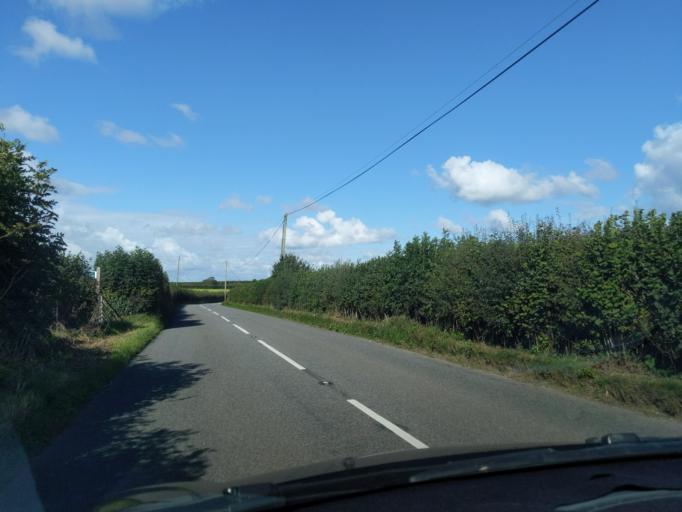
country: GB
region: England
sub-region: Cornwall
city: Boyton
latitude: 50.7270
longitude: -4.3276
